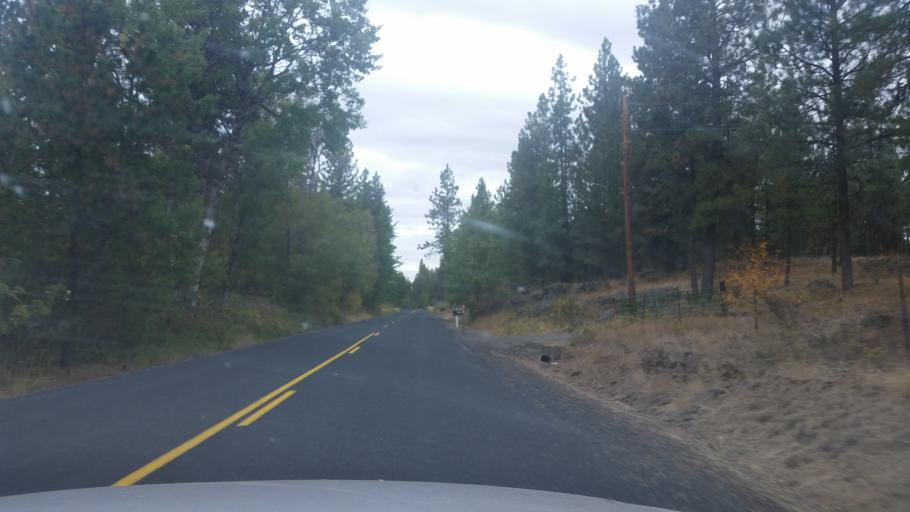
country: US
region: Washington
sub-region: Spokane County
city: Medical Lake
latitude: 47.4897
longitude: -117.7745
